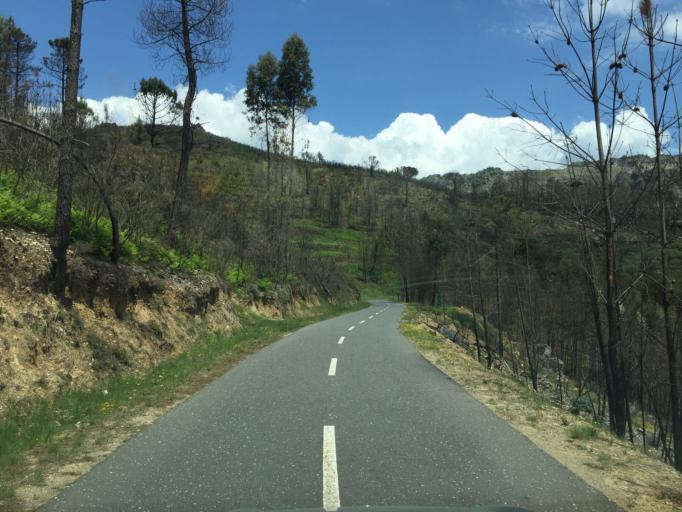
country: PT
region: Coimbra
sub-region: Pampilhosa da Serra
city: Pampilhosa da Serra
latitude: 40.0888
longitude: -7.8719
